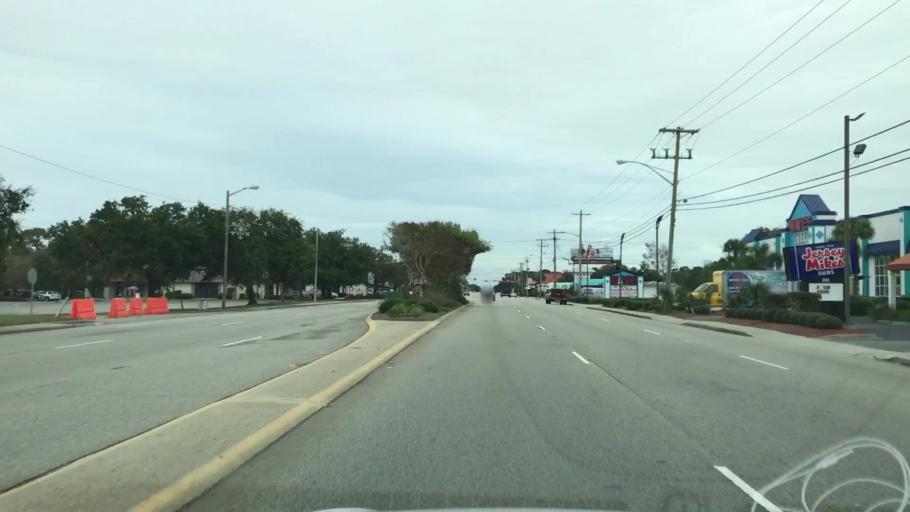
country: US
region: South Carolina
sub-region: Horry County
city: Myrtle Beach
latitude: 33.7069
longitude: -78.8666
